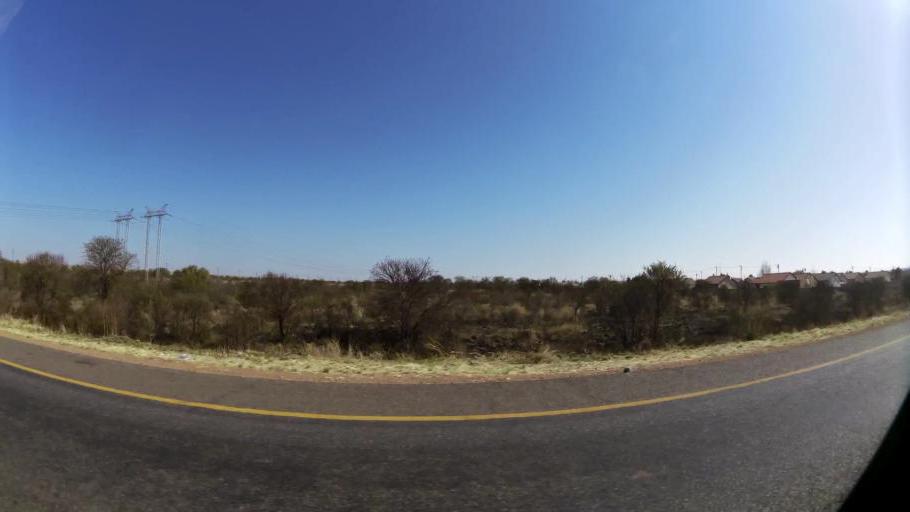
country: ZA
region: Gauteng
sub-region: City of Tshwane Metropolitan Municipality
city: Mabopane
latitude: -25.6063
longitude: 28.1137
